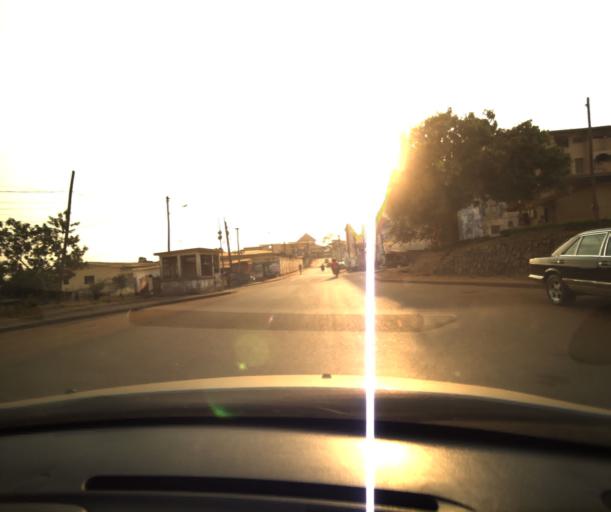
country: CM
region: Centre
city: Yaounde
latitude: 3.8768
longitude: 11.4904
